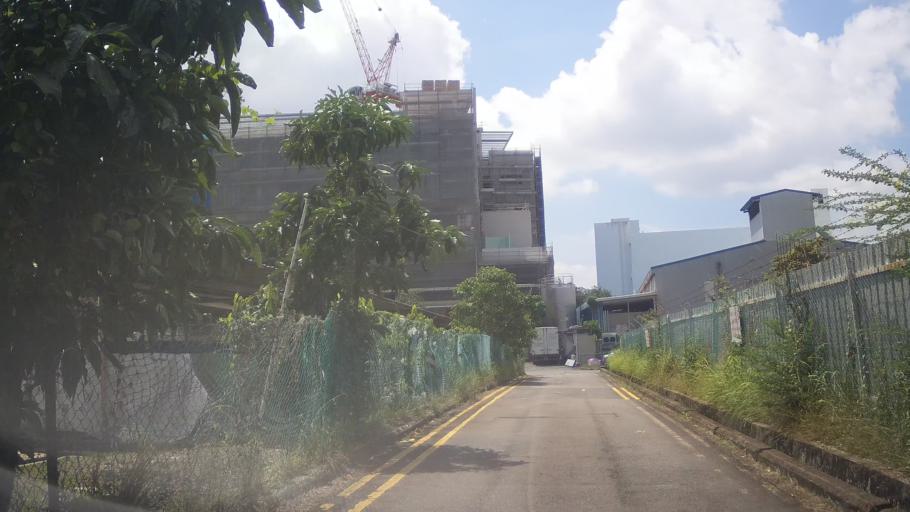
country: MY
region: Johor
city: Johor Bahru
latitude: 1.3375
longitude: 103.7134
